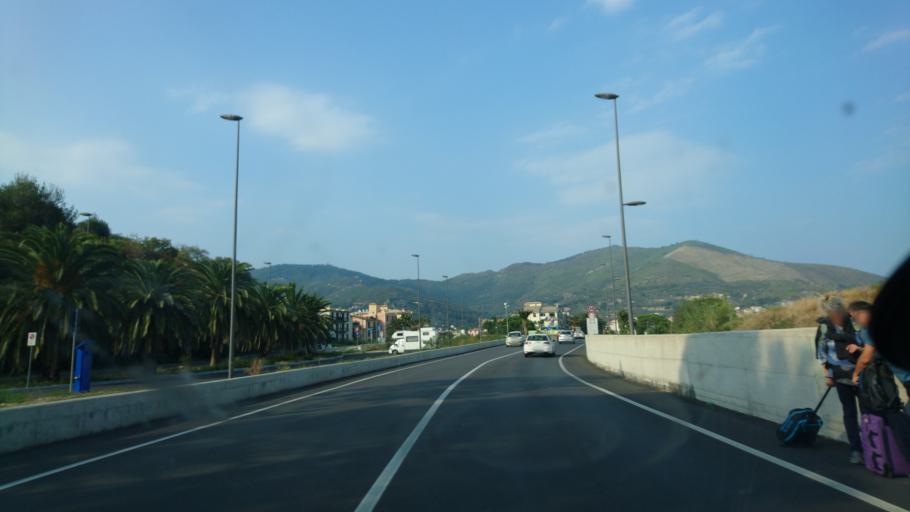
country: IT
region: Liguria
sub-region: Provincia di Savona
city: Spotorno
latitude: 44.2187
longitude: 8.4147
